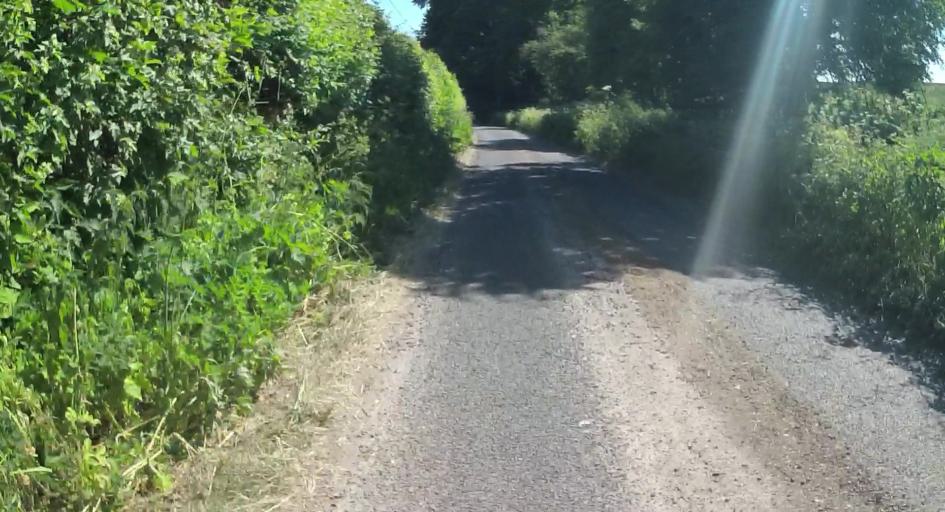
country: GB
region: England
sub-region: Hampshire
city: Overton
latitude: 51.2929
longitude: -1.3034
